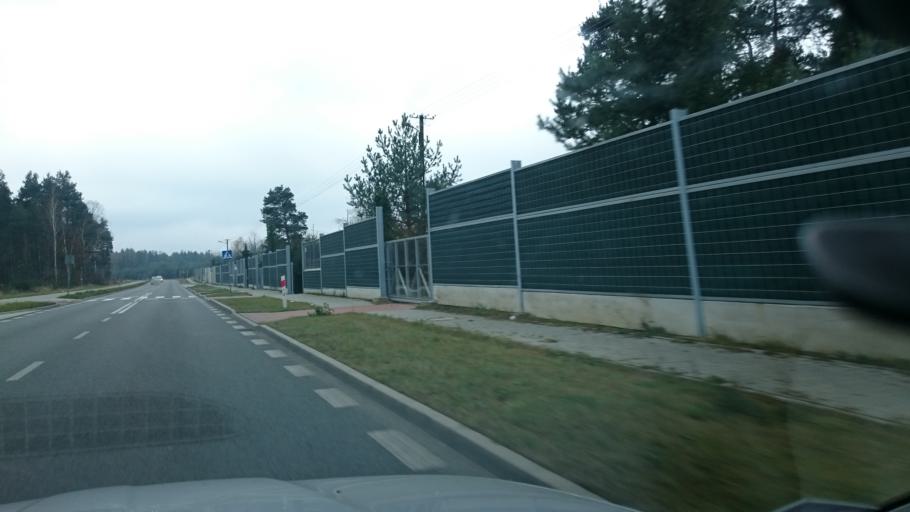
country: PL
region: Swietokrzyskie
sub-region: Powiat konecki
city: Konskie
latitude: 51.1548
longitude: 20.3640
